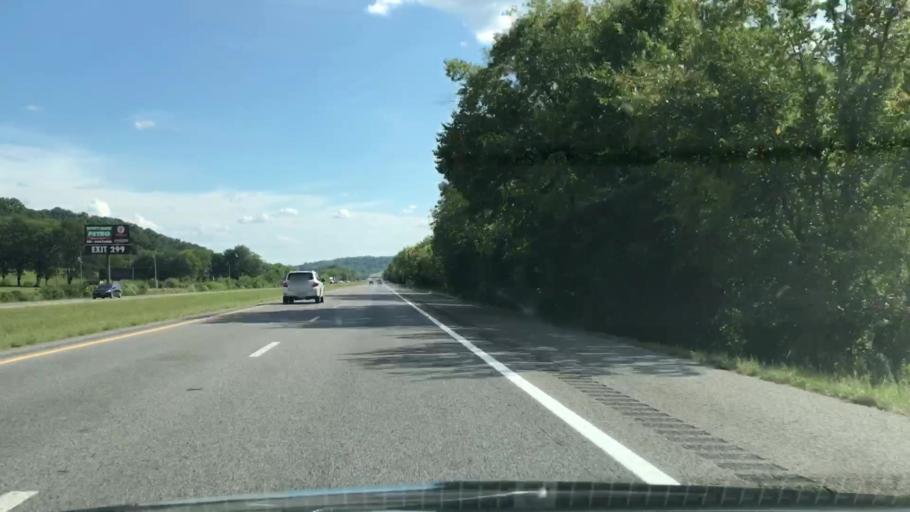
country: US
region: Tennessee
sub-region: Giles County
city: Pulaski
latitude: 35.1534
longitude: -86.8796
